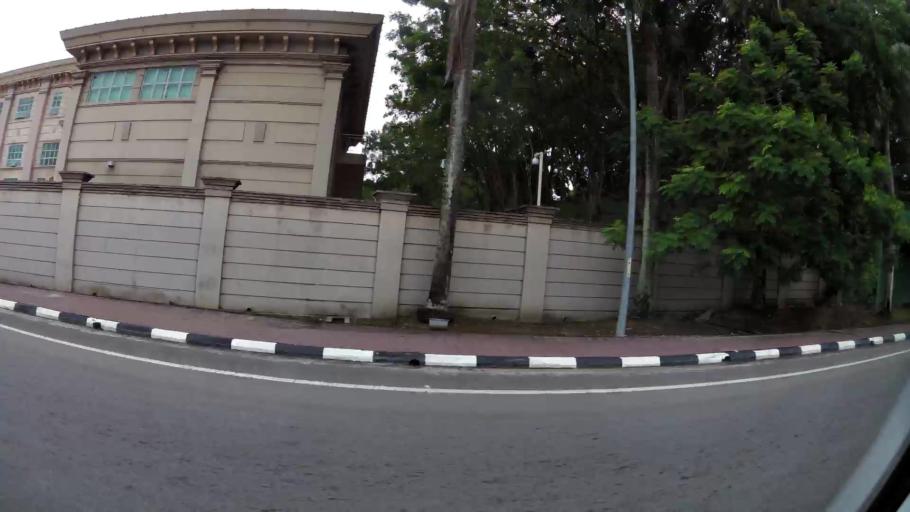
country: BN
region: Brunei and Muara
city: Bandar Seri Begawan
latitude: 4.8894
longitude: 114.9338
